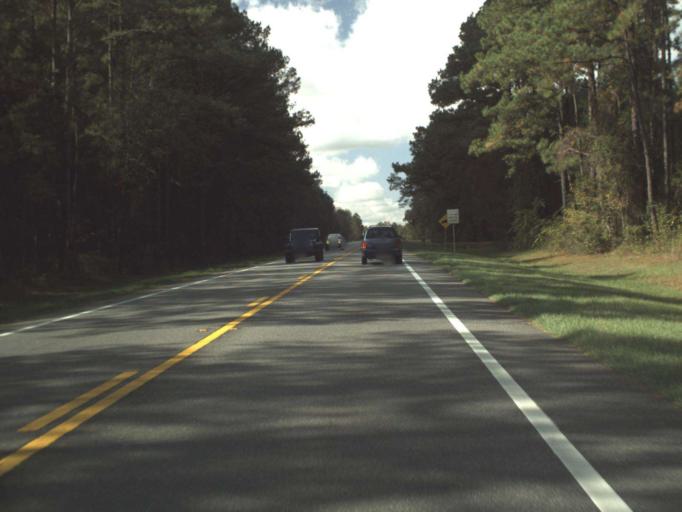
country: US
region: Florida
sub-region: Jackson County
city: Marianna
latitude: 30.7404
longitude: -85.1344
